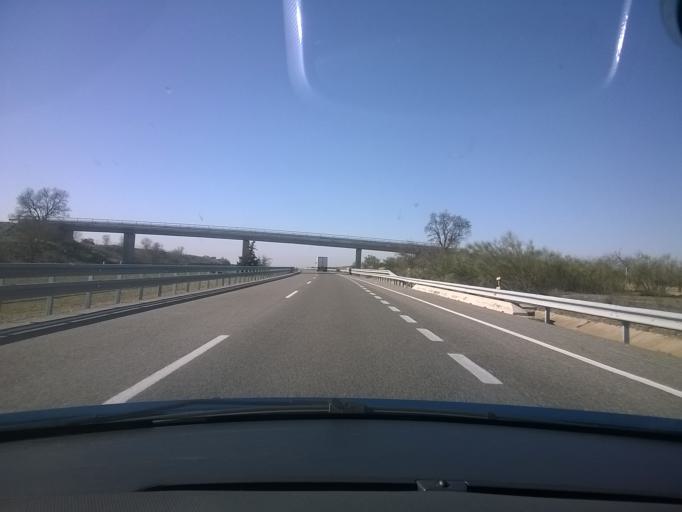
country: ES
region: Aragon
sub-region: Provincia de Huesca
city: Fraga
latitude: 41.4680
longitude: 0.2655
